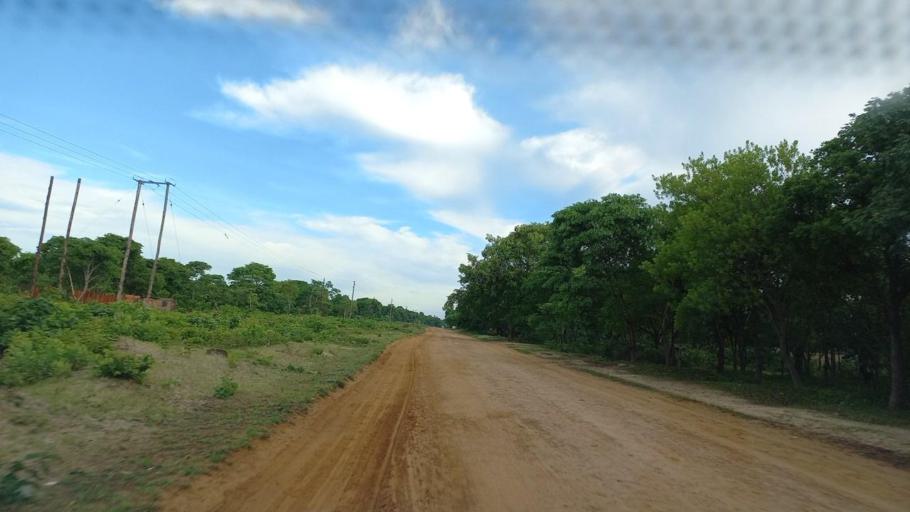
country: ZM
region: North-Western
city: Kabompo
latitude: -13.4071
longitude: 24.3132
